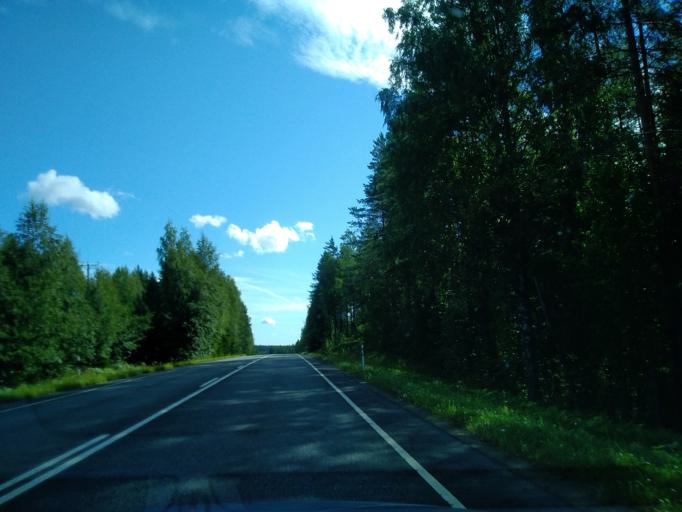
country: FI
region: Uusimaa
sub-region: Helsinki
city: Kaerkoelae
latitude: 60.8293
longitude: 24.0324
